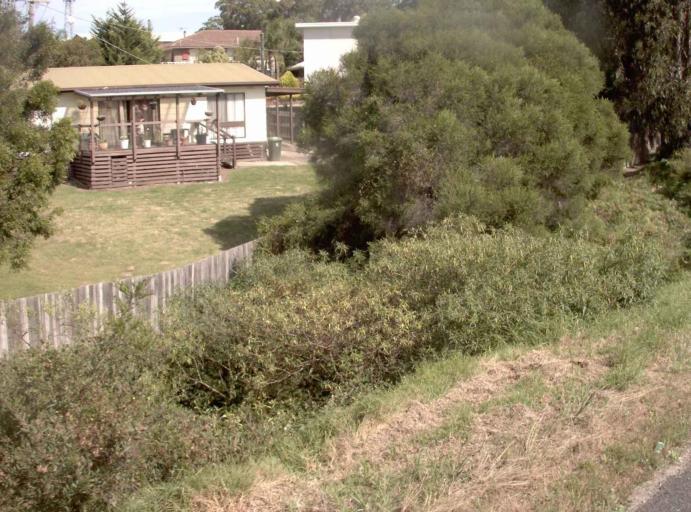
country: AU
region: Victoria
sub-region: East Gippsland
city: Lakes Entrance
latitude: -37.8764
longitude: 147.9612
